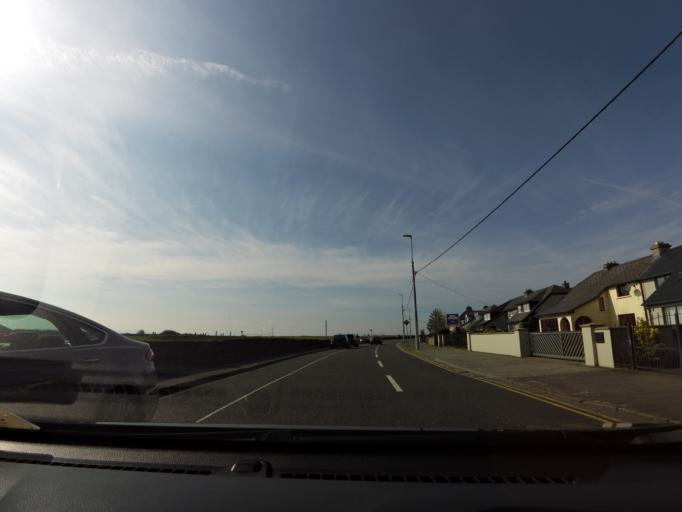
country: IE
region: Connaught
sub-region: County Galway
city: Gaillimh
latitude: 53.2646
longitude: -9.0560
